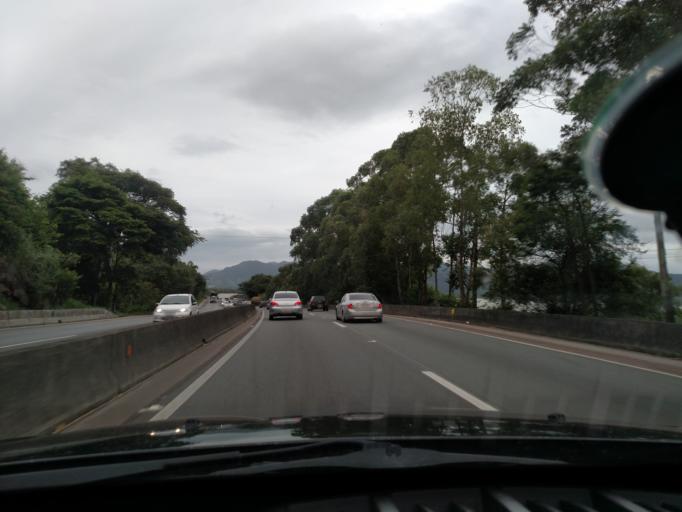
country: BR
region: Santa Catarina
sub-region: Biguacu
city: Biguacu
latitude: -27.4431
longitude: -48.6284
